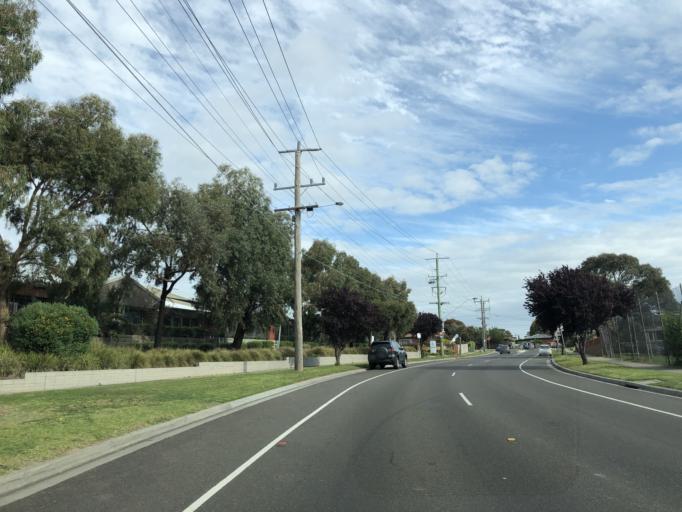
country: AU
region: Victoria
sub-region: Greater Dandenong
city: Noble Park North
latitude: -37.9538
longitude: 145.1965
